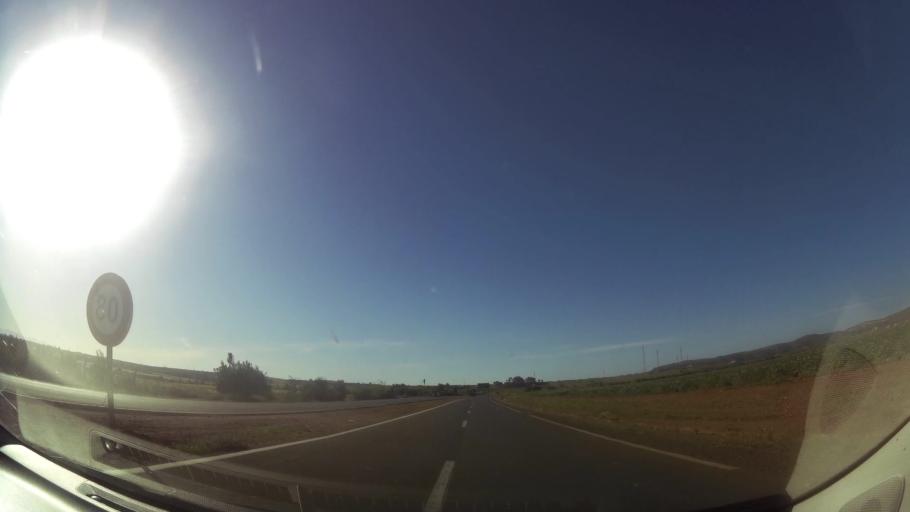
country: MA
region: Oriental
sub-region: Berkane-Taourirt
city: Ahfir
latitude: 35.0250
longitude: -2.2056
